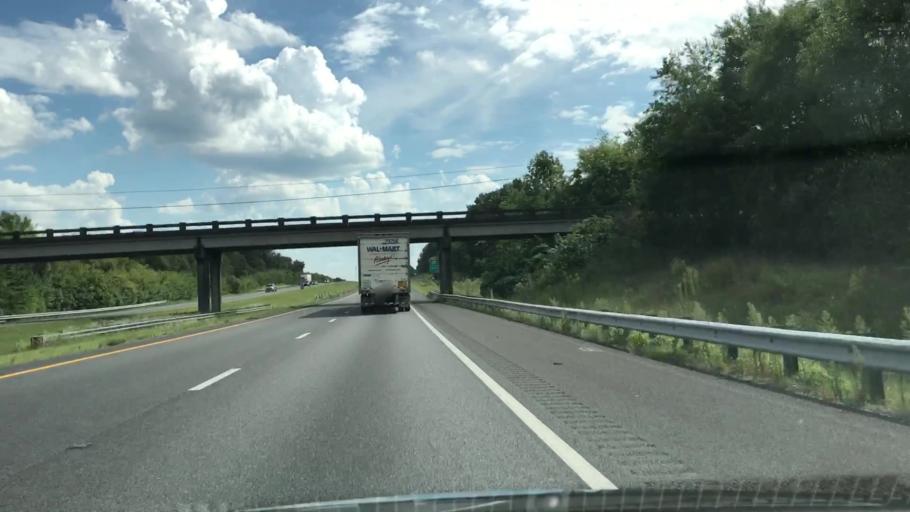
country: US
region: Tennessee
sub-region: Maury County
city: Spring Hill
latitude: 35.6613
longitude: -86.8926
